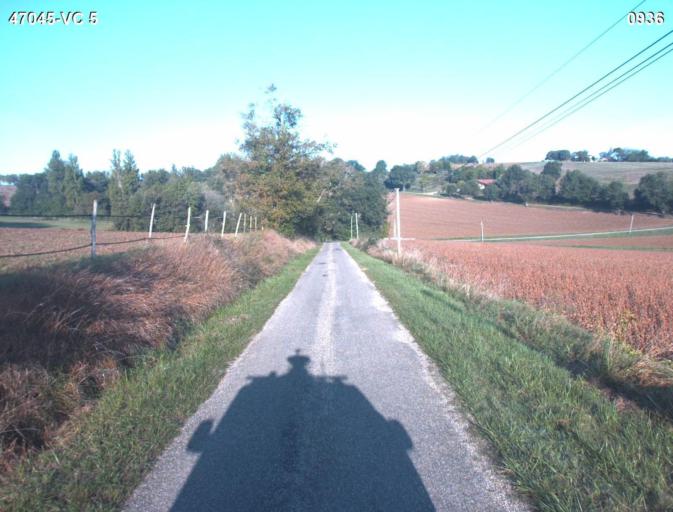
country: FR
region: Aquitaine
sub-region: Departement du Lot-et-Garonne
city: Nerac
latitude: 44.1385
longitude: 0.4059
